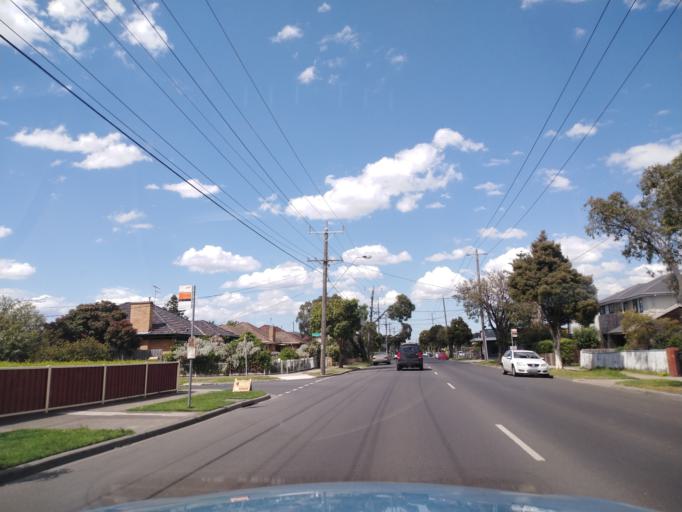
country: AU
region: Victoria
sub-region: Hobsons Bay
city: South Kingsville
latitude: -37.8333
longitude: 144.8679
